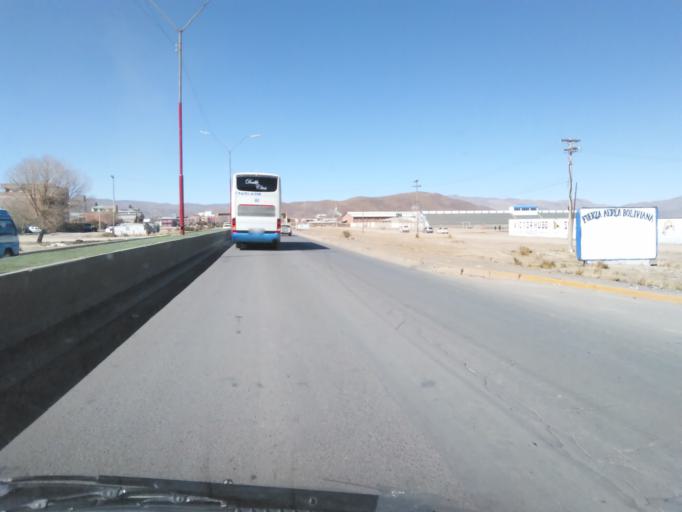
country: BO
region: Oruro
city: Oruro
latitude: -17.9751
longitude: -67.0749
